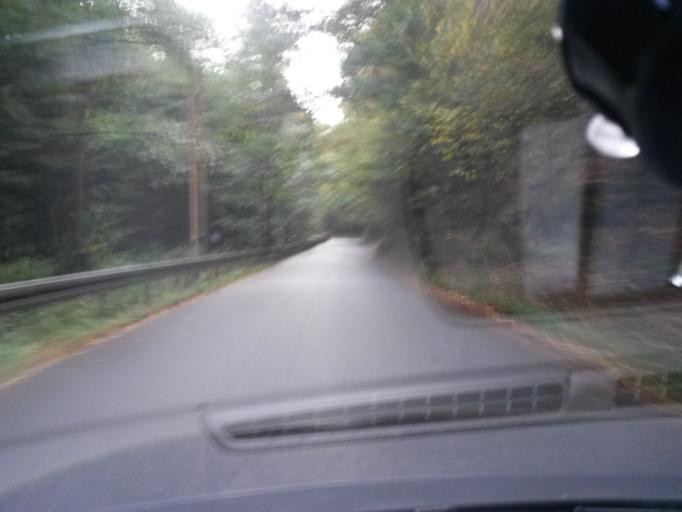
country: DE
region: North Rhine-Westphalia
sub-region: Regierungsbezirk Arnsberg
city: Herscheid
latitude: 51.2132
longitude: 7.7240
